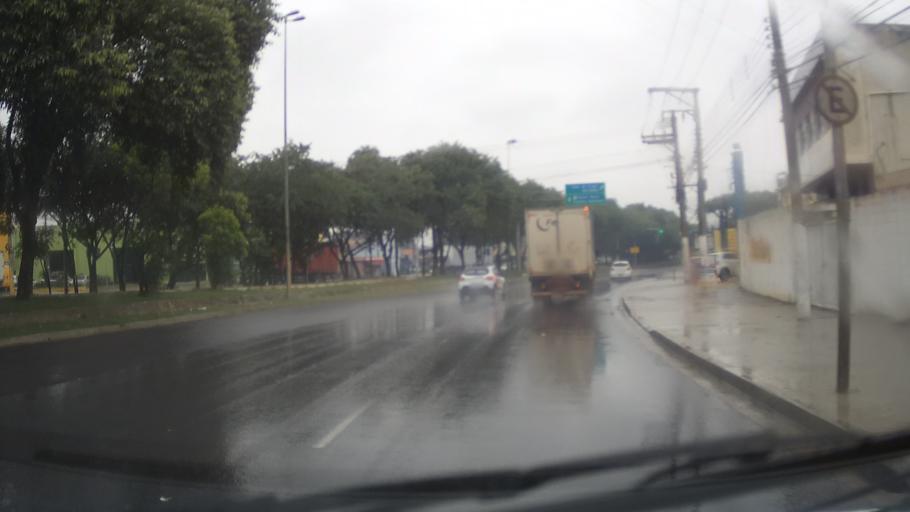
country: BR
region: Sao Paulo
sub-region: Guarulhos
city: Guarulhos
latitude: -23.4687
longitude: -46.4659
